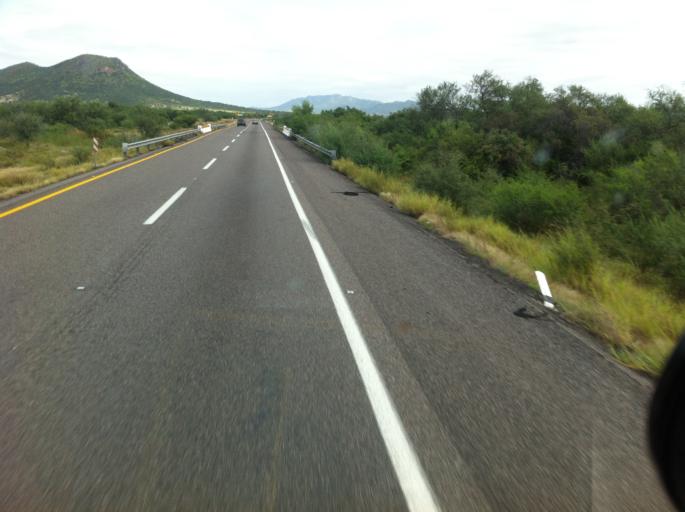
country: MX
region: Sonora
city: Hermosillo
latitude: 28.8685
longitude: -110.9585
